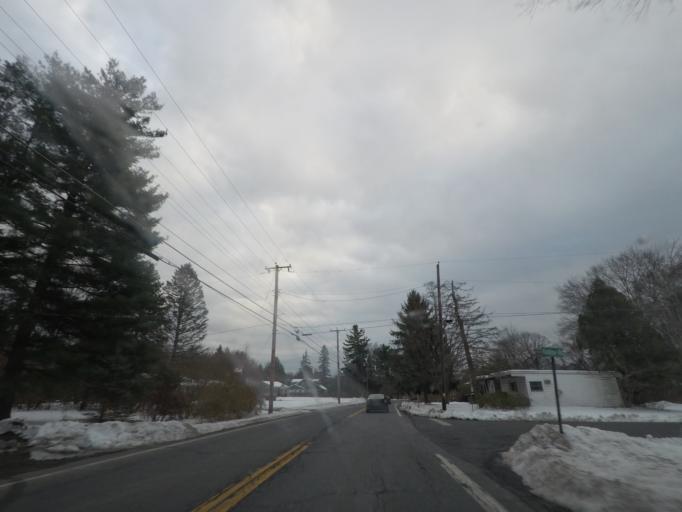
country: US
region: New York
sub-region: Ulster County
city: New Paltz
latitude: 41.7108
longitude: -74.0874
